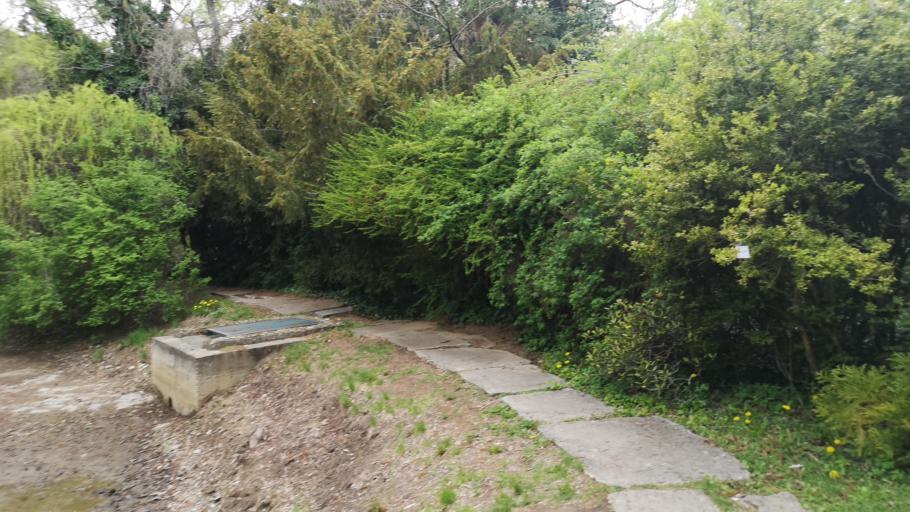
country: SK
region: Nitriansky
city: Zlate Moravce
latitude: 48.3161
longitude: 18.3678
